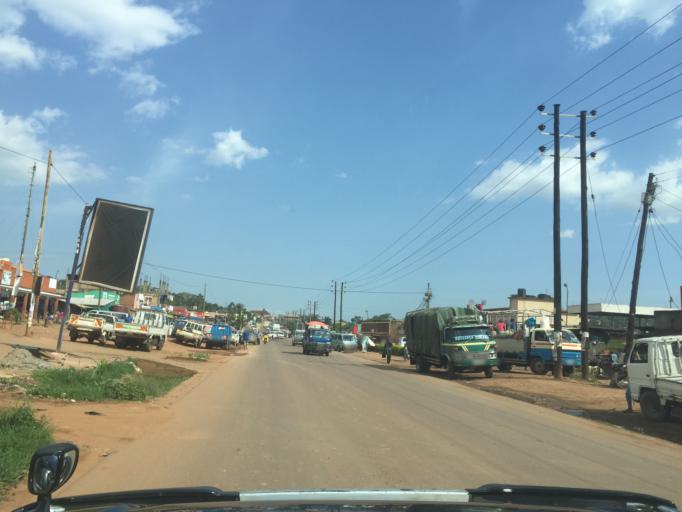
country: UG
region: Central Region
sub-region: Wakiso District
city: Wakiso
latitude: 0.4665
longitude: 32.5202
